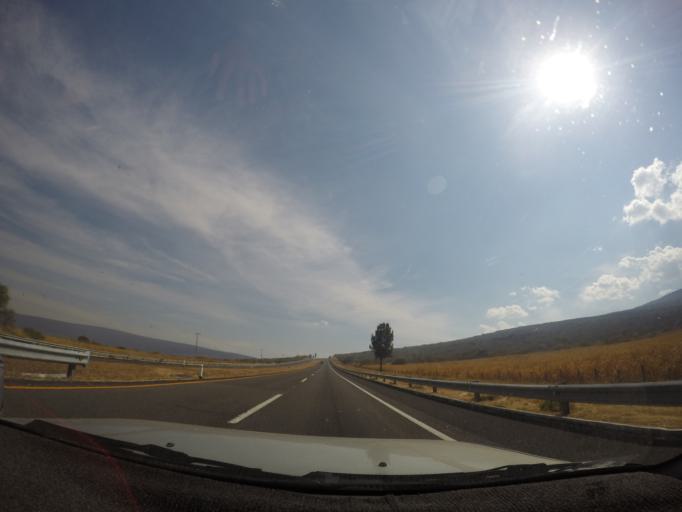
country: MX
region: Michoacan
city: Churintzio
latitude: 20.1535
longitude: -102.1032
